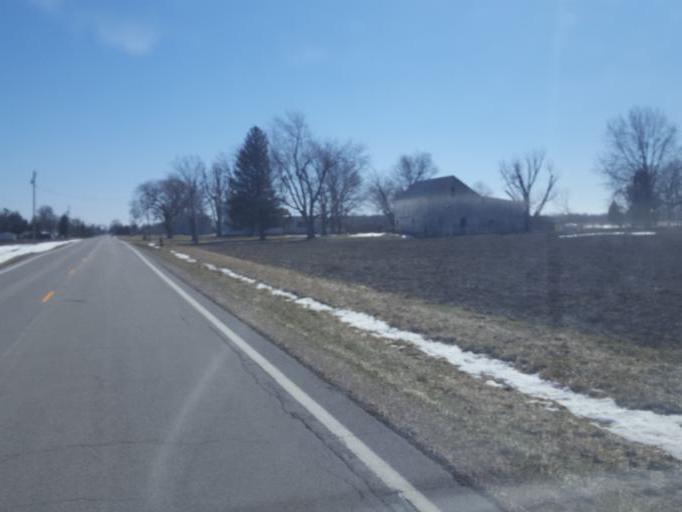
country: US
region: Ohio
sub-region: Wyandot County
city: Upper Sandusky
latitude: 40.7380
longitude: -83.2694
